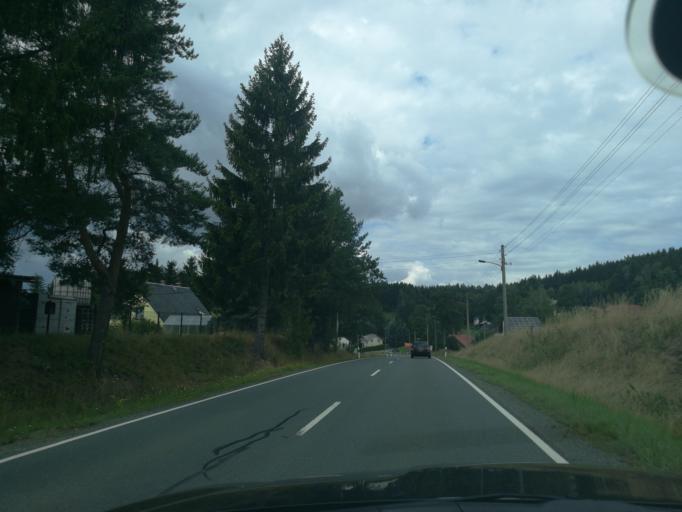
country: DE
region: Saxony
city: Adorf
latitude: 50.3617
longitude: 12.2246
